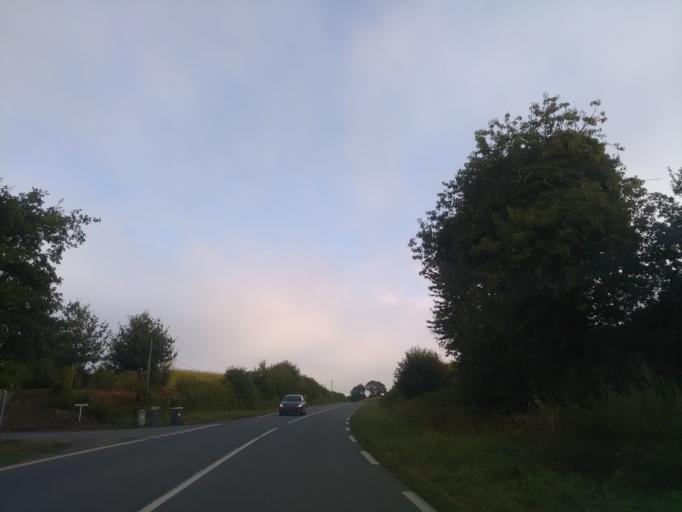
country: FR
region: Brittany
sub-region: Departement d'Ille-et-Vilaine
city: Geveze
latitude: 48.2356
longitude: -1.8060
